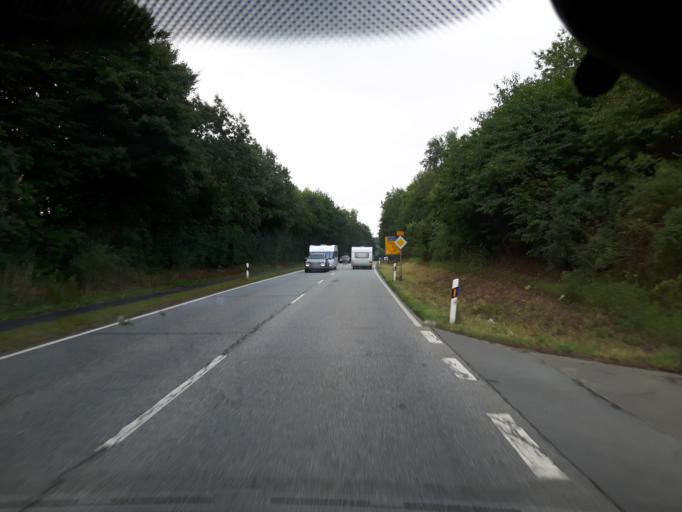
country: DE
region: Schleswig-Holstein
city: Holzbunge
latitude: 54.3616
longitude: 9.7048
